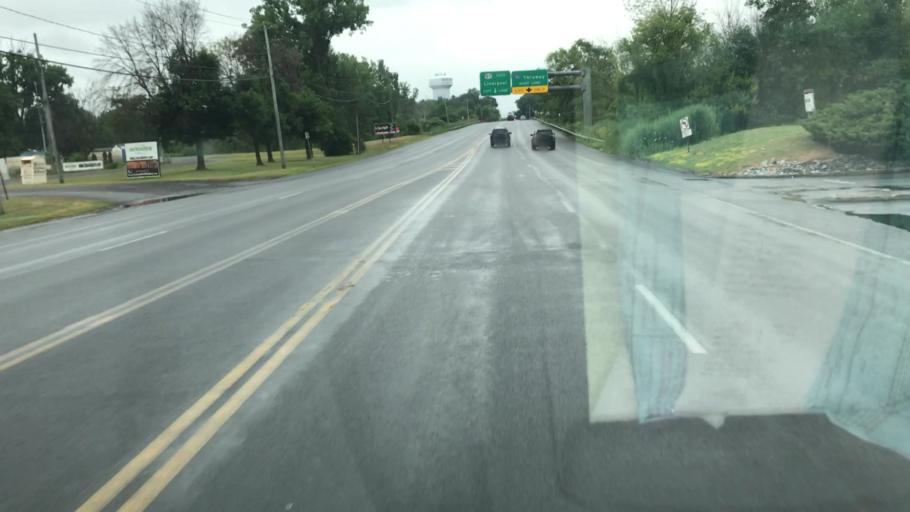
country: US
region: New York
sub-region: Onondaga County
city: Liverpool
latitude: 43.1188
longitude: -76.2147
